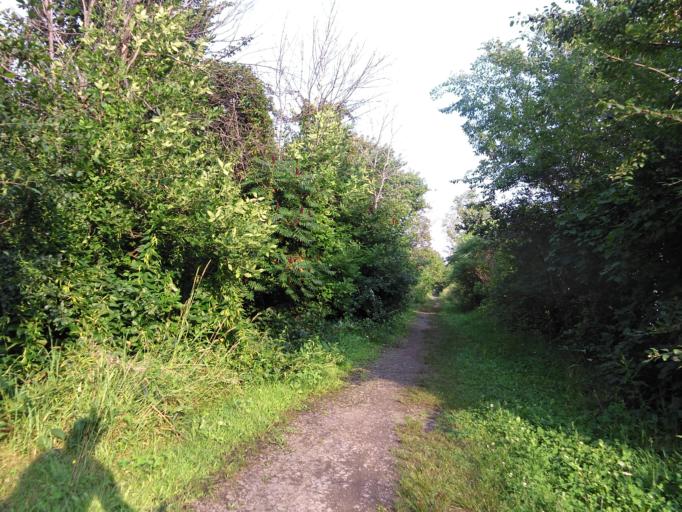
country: CA
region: Ontario
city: Bells Corners
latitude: 45.4050
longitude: -75.8690
